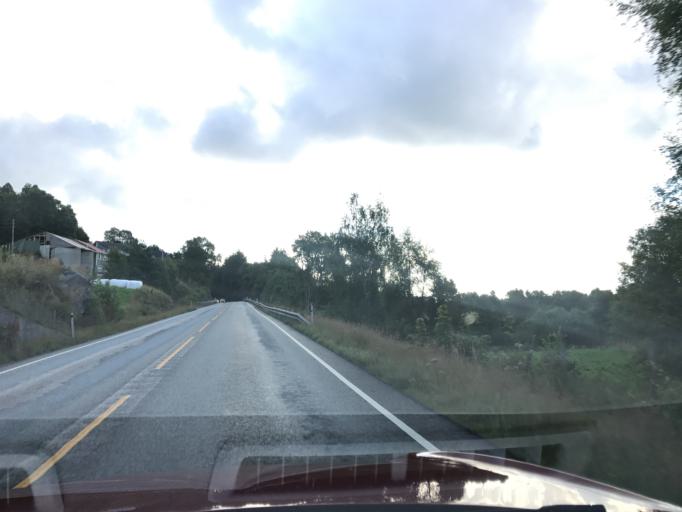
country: NO
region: Hordaland
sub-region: Sveio
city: Sveio
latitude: 59.5408
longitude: 5.3552
